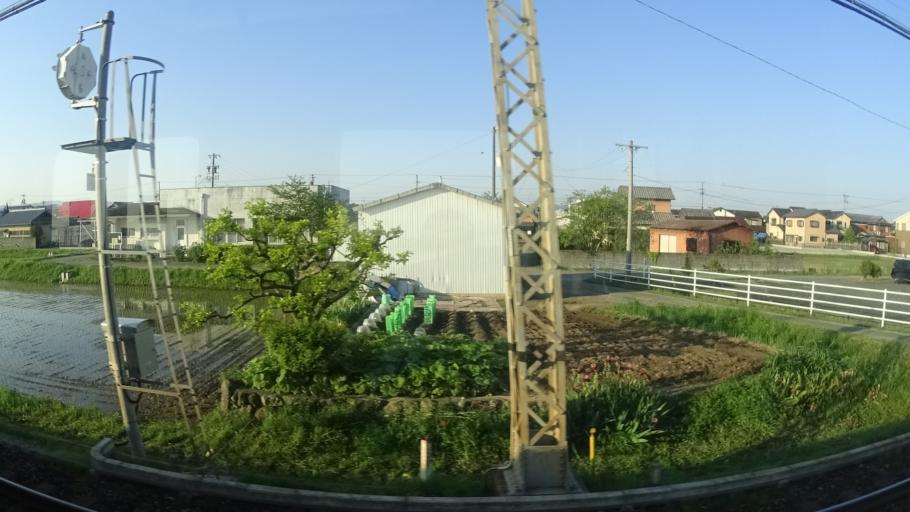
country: JP
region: Mie
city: Ise
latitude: 34.5368
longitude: 136.6268
